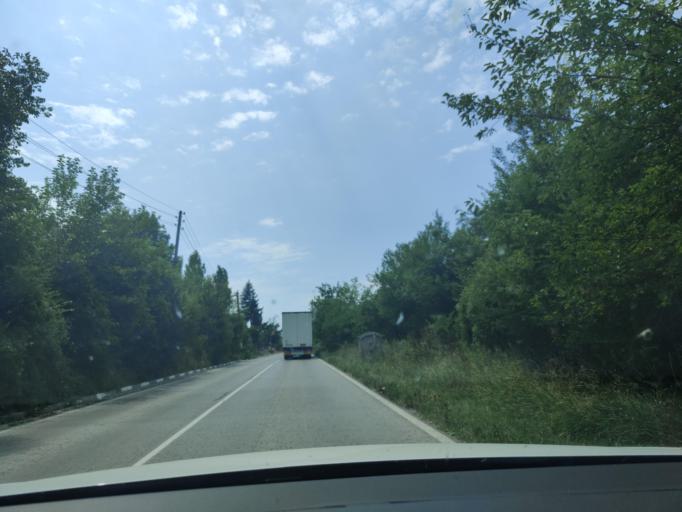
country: BG
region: Vidin
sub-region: Obshtina Ruzhintsi
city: Ruzhintsi
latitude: 43.6539
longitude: 22.7897
